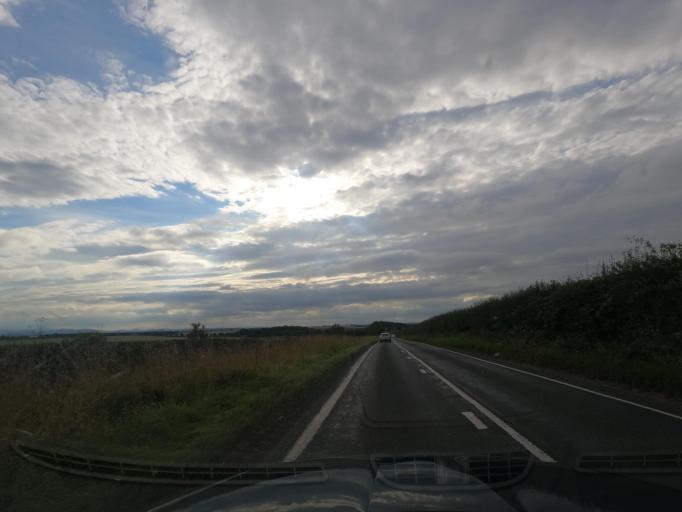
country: GB
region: England
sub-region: Northumberland
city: Ford
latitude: 55.7082
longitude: -2.1370
